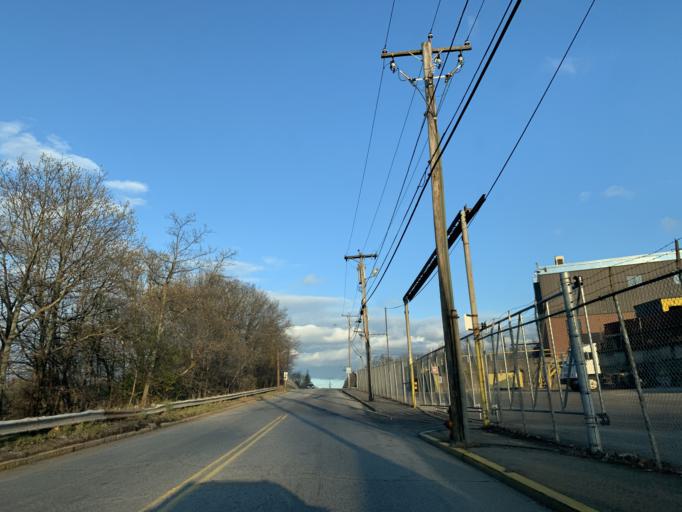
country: US
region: Rhode Island
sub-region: Providence County
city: Valley Falls
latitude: 41.8975
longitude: -71.3750
